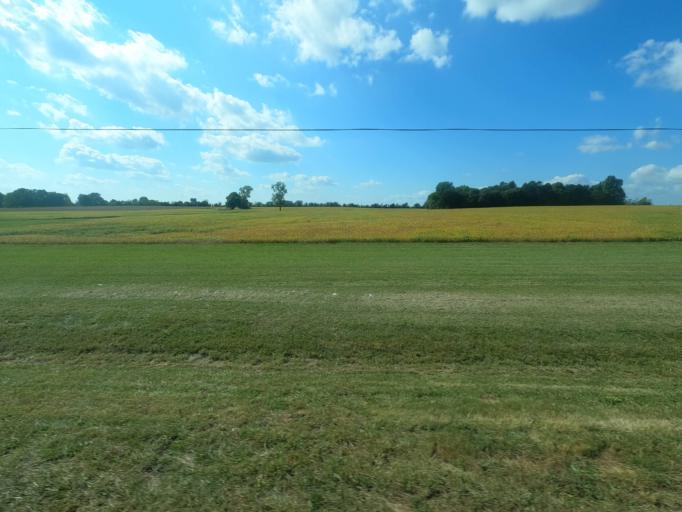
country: US
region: Illinois
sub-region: Massac County
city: Metropolis
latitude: 37.1847
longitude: -88.6766
